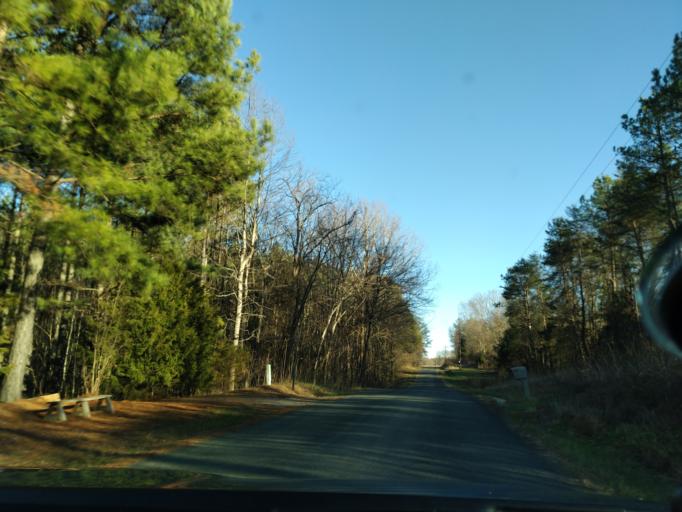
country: US
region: Virginia
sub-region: Buckingham County
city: Buckingham
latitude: 37.3724
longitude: -78.6287
